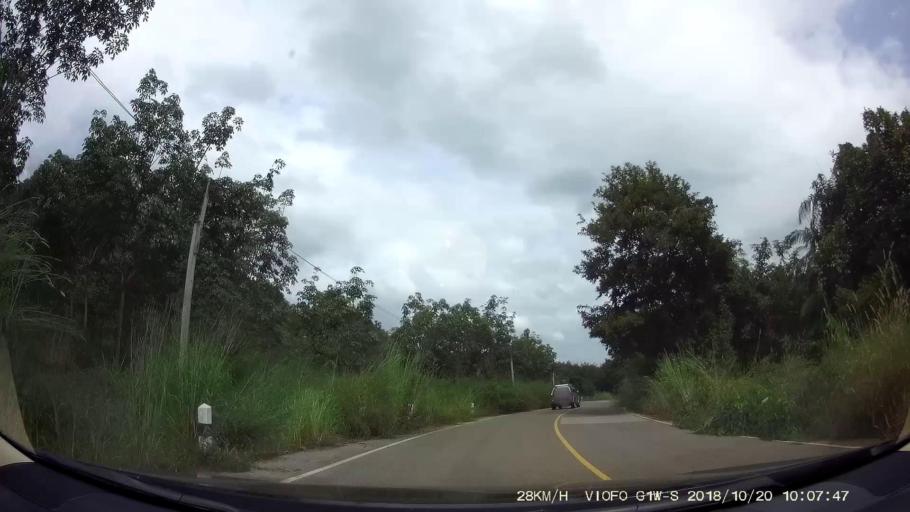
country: TH
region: Chaiyaphum
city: Khon San
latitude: 16.5495
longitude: 101.8523
